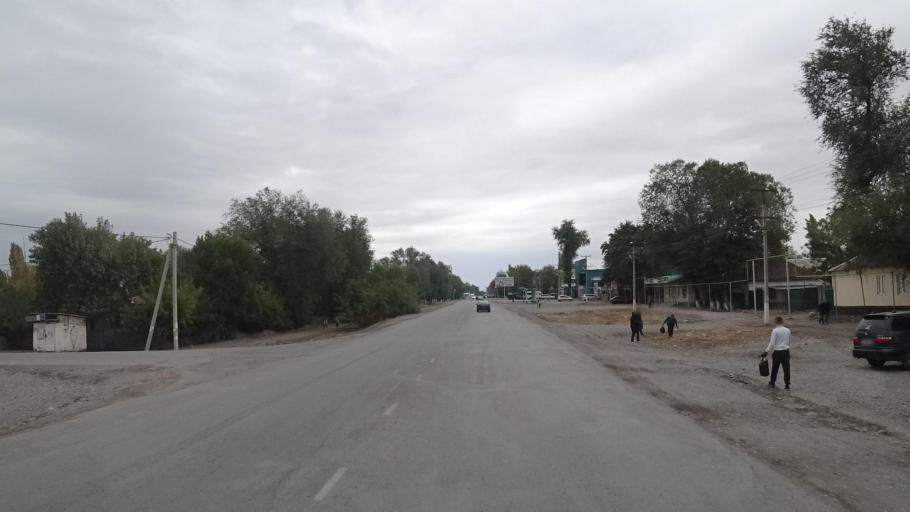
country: KG
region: Chuy
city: Kara-Balta
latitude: 42.8264
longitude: 73.8572
